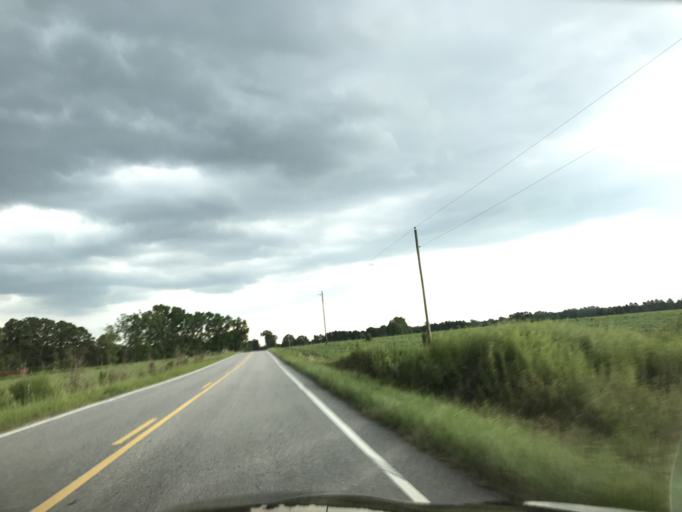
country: US
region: North Carolina
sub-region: Johnston County
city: Four Oaks
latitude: 35.5235
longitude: -78.4593
